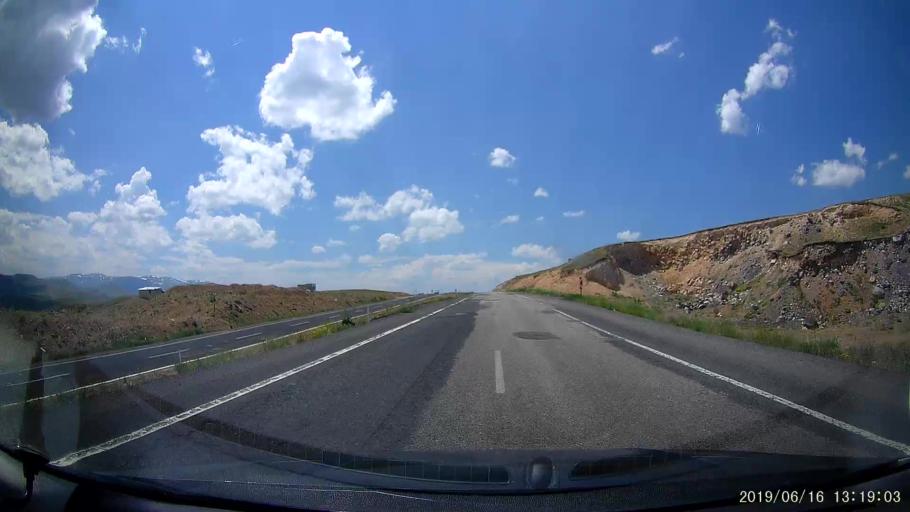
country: TR
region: Agri
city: Taslicay
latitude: 39.6325
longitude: 43.4168
